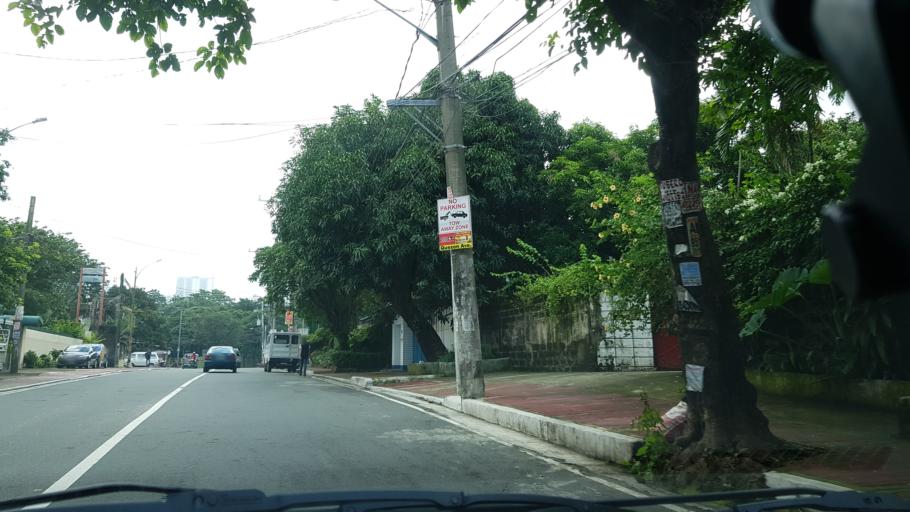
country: PH
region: Calabarzon
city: Del Monte
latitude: 14.6304
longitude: 121.0197
